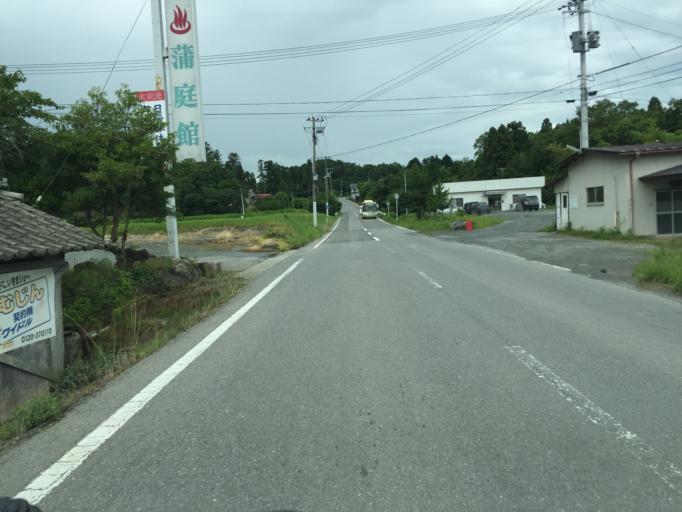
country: JP
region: Fukushima
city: Namie
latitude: 37.7437
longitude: 141.0037
